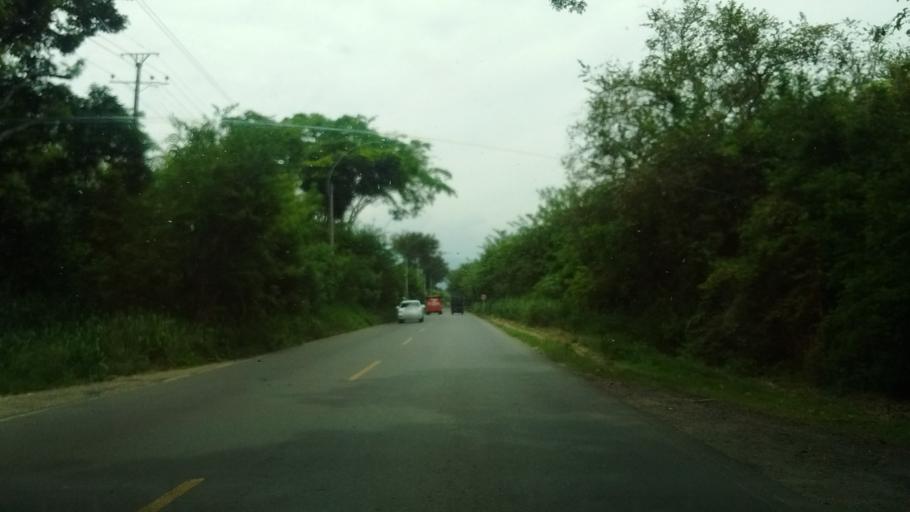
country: CO
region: Valle del Cauca
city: Jamundi
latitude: 3.3396
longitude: -76.5194
